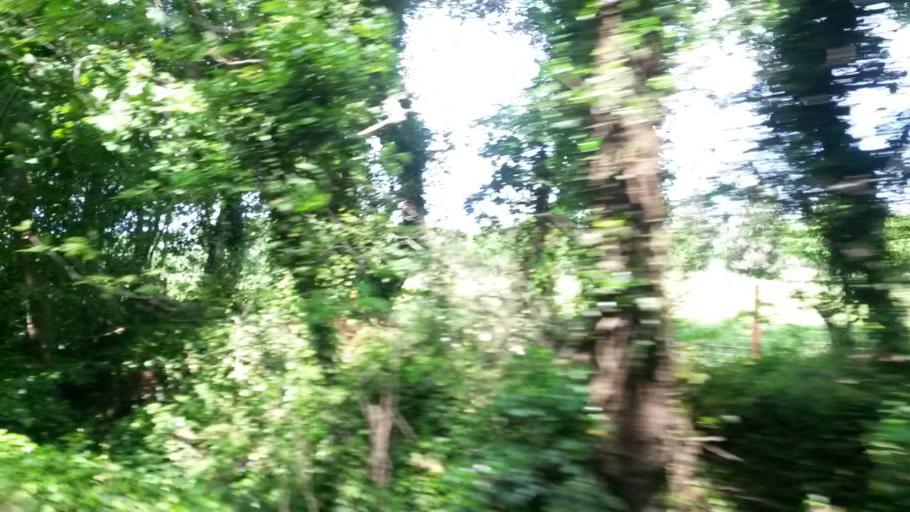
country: IE
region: Leinster
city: Donabate
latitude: 53.4903
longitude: -6.1710
